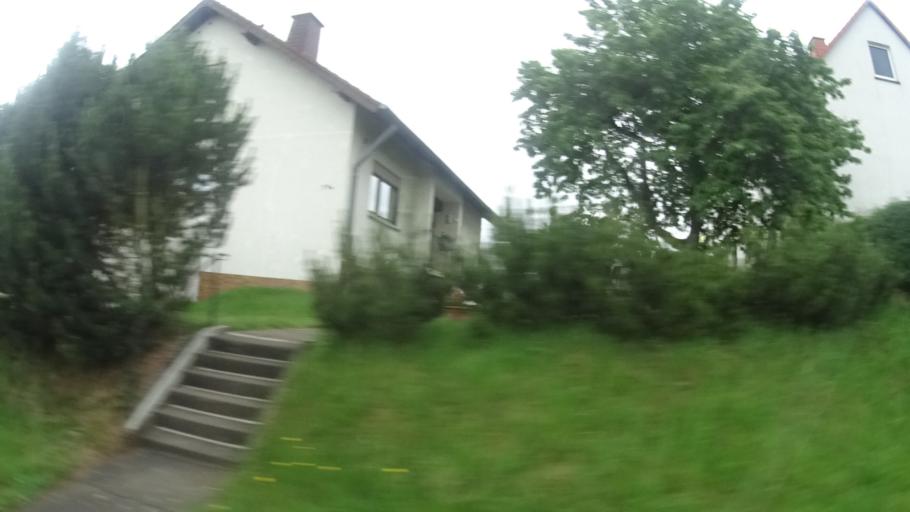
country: DE
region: Hesse
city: Tann
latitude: 50.6161
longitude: 10.0300
